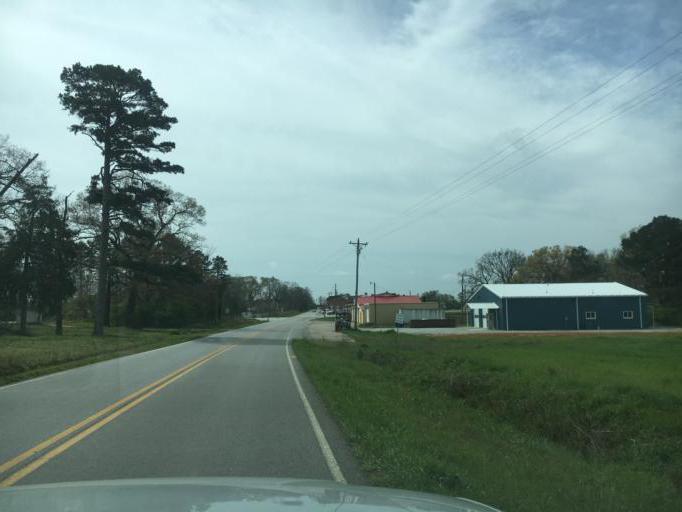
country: US
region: Georgia
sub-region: Hart County
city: Royston
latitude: 34.2920
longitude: -83.0461
